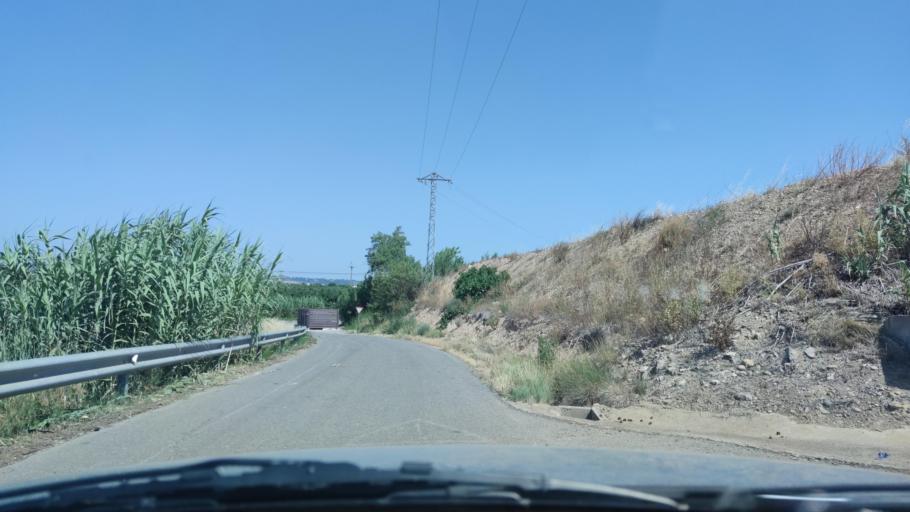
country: ES
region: Catalonia
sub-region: Provincia de Lleida
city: Torrefarrera
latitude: 41.6419
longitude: 0.5879
